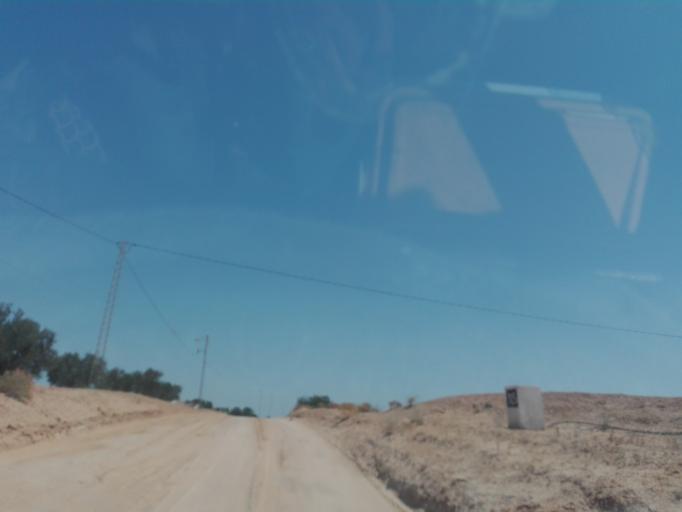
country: TN
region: Safaqis
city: Bi'r `Ali Bin Khalifah
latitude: 34.6707
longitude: 10.2353
